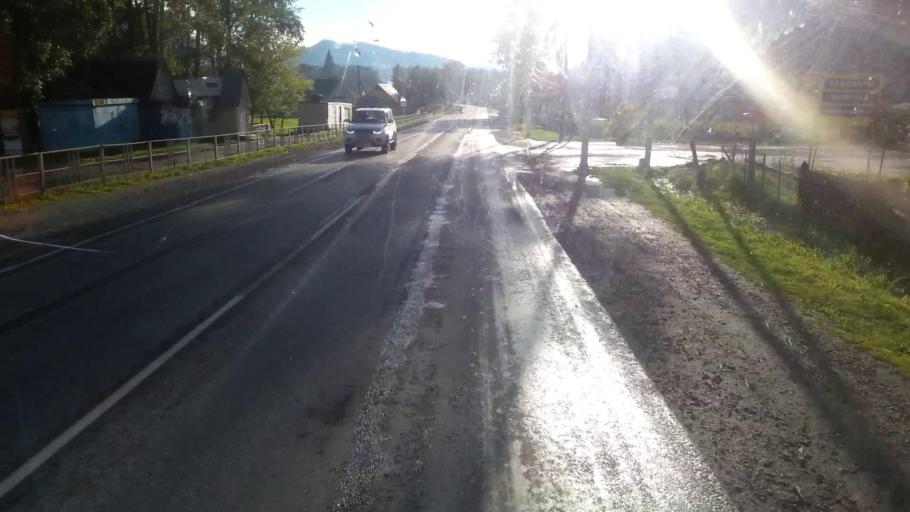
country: RU
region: Altay
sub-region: Mayminskiy Rayon
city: Manzherok
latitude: 51.8338
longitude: 85.7779
